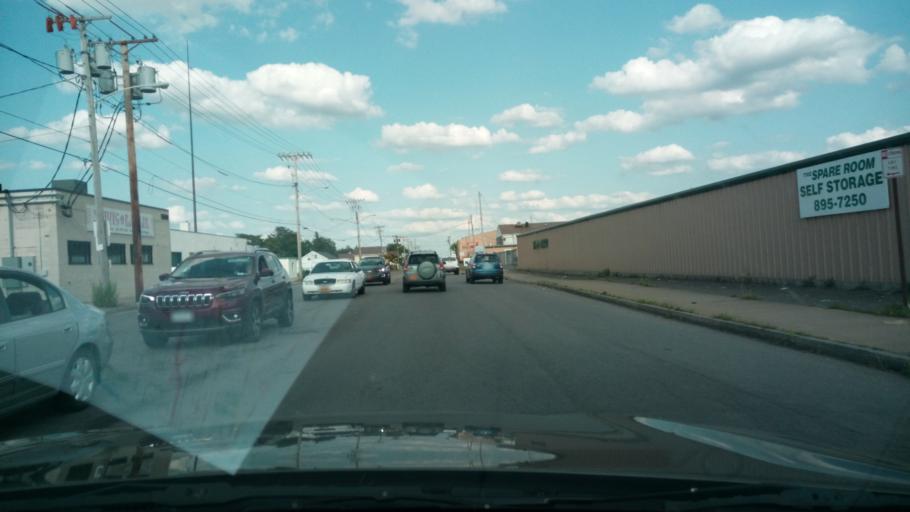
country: US
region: New York
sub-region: Erie County
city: Sloan
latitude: 42.8847
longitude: -78.8140
